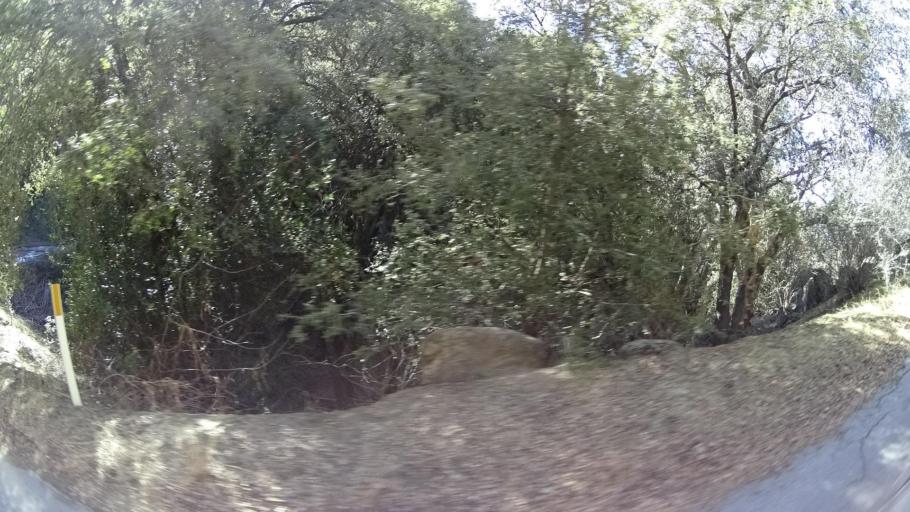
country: US
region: California
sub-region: Kern County
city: Bodfish
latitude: 35.4646
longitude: -118.6476
